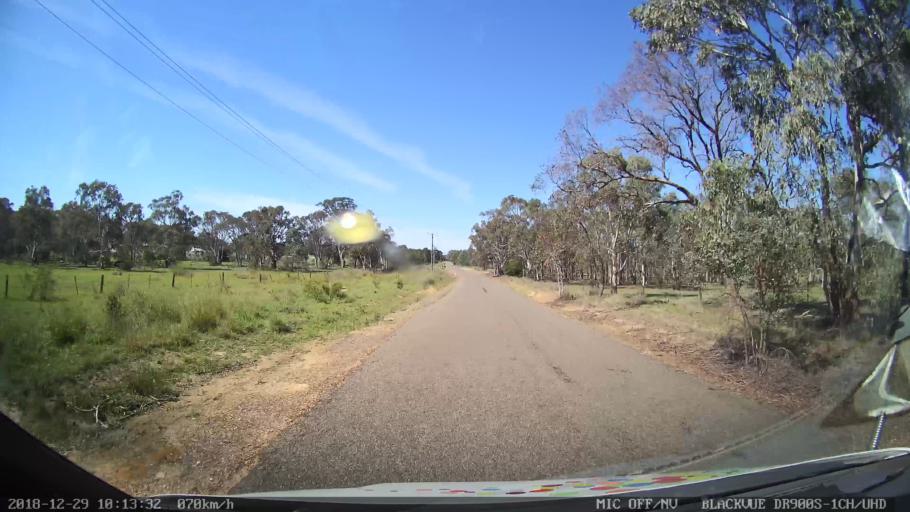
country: AU
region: New South Wales
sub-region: Yass Valley
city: Gundaroo
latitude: -34.9042
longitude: 149.4433
